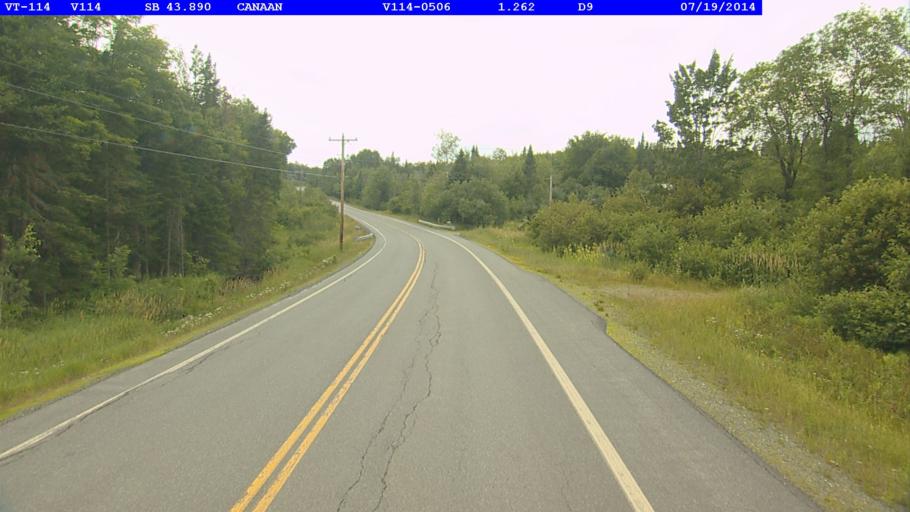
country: CA
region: Quebec
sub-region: Estrie
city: Coaticook
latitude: 45.0062
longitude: -71.6682
